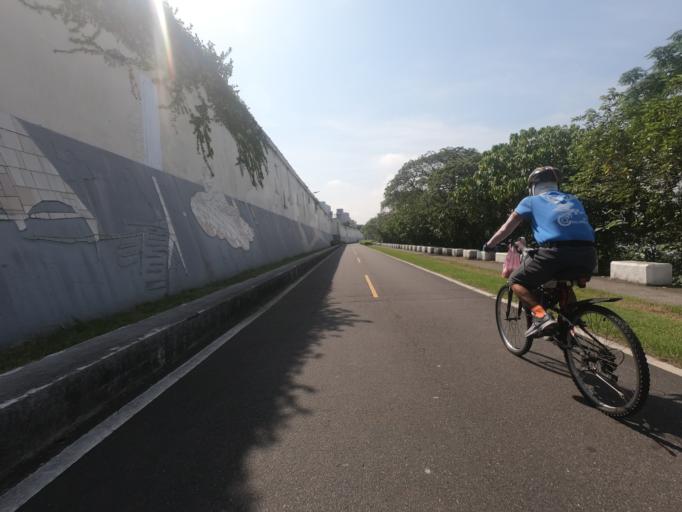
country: TW
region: Taipei
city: Taipei
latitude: 25.0910
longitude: 121.4999
